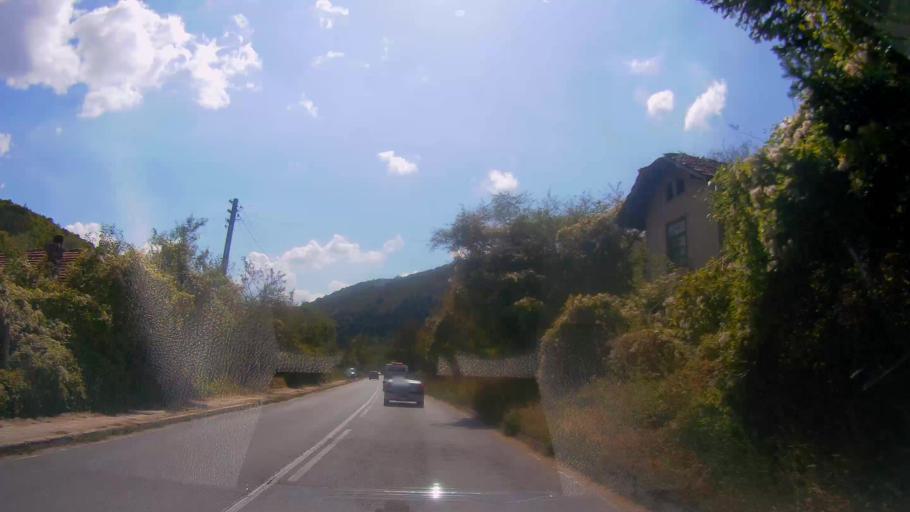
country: BG
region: Stara Zagora
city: Gurkovo
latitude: 42.7400
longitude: 25.7081
